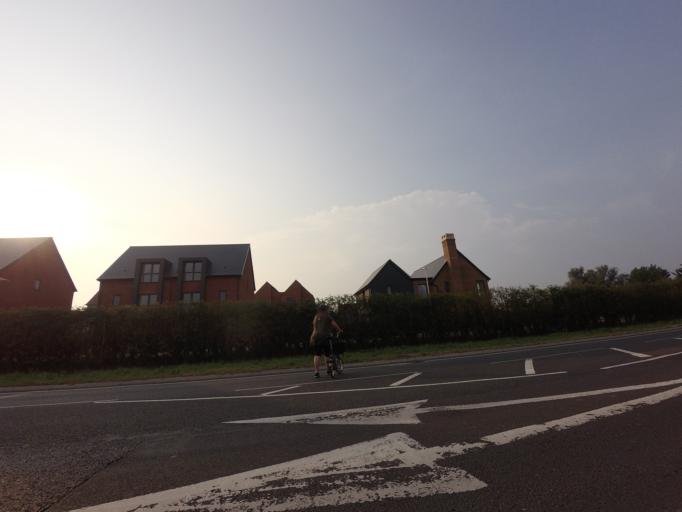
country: GB
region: England
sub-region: Kent
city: Ashford
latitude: 51.1353
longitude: 0.8196
